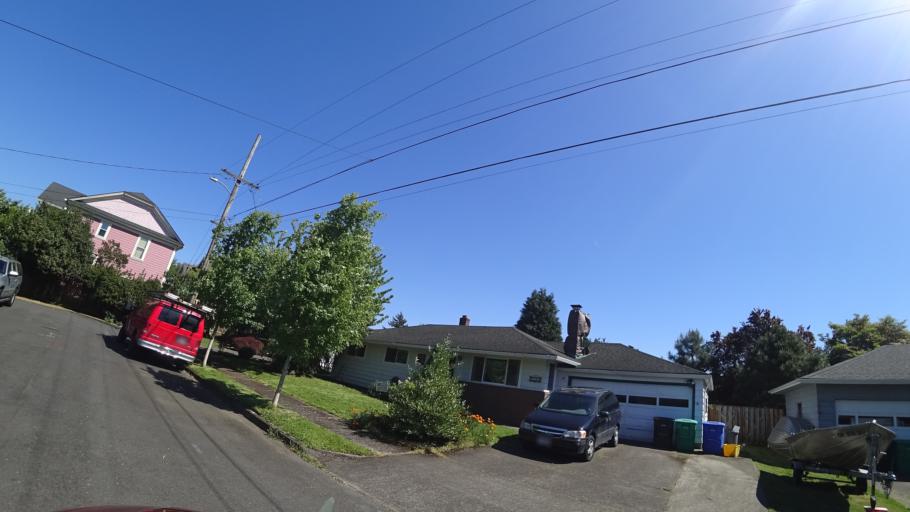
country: US
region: Oregon
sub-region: Multnomah County
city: Lents
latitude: 45.5010
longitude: -122.6142
